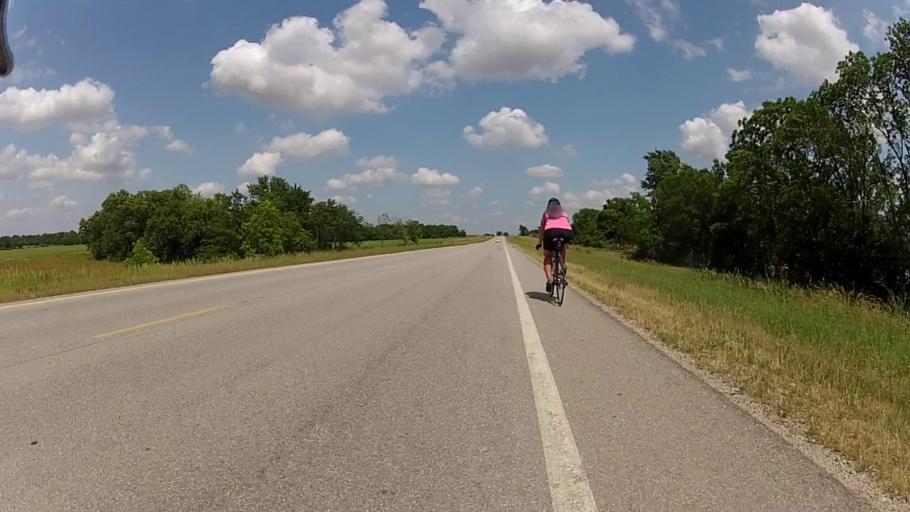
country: US
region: Kansas
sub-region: Labette County
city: Oswego
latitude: 37.1938
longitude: -95.1897
